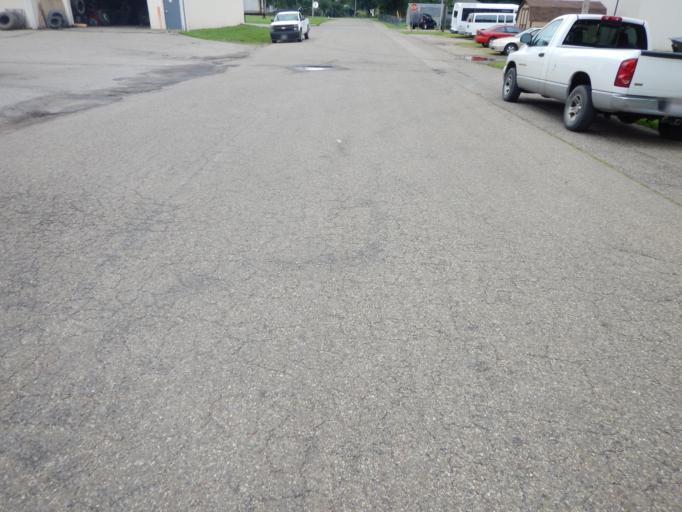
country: US
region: Ohio
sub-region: Muskingum County
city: Zanesville
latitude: 39.9456
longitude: -82.0187
